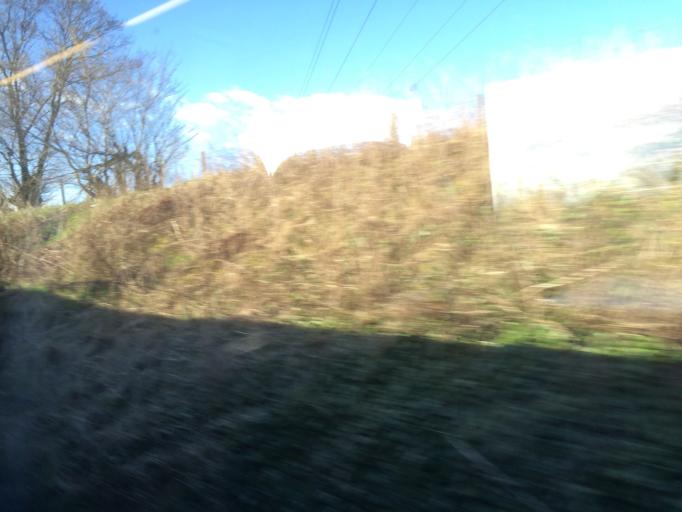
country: GB
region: Scotland
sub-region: Stirling
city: Plean
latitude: 56.0859
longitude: -3.8856
